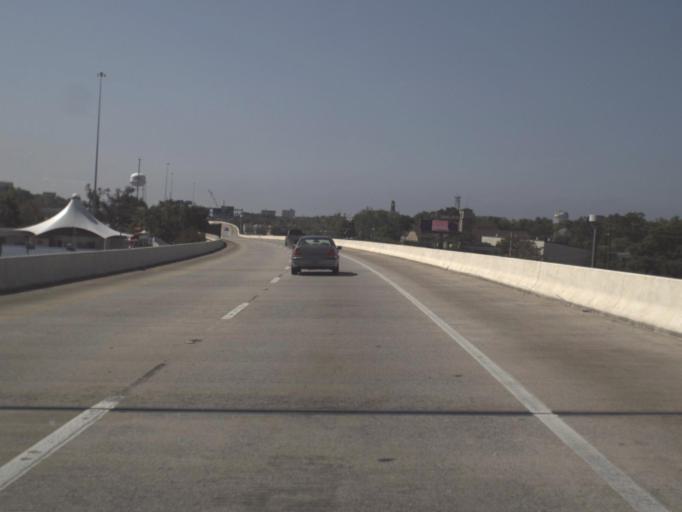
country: US
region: Florida
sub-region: Escambia County
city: Pensacola
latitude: 30.4307
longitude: -87.2162
